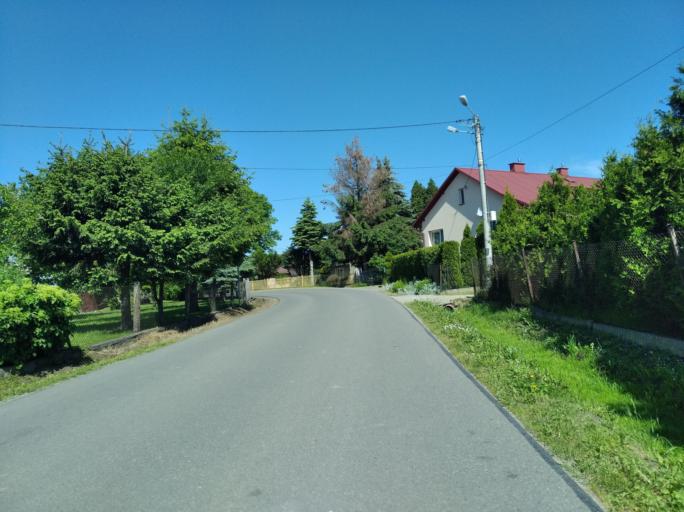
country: PL
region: Subcarpathian Voivodeship
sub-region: Krosno
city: Krosno
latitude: 49.7213
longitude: 21.7701
